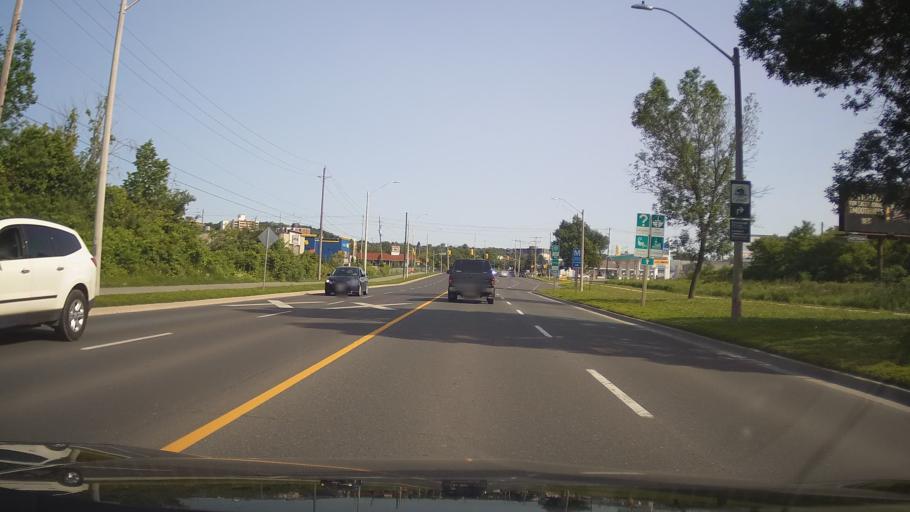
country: CA
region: Ontario
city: Peterborough
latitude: 44.2803
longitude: -78.3429
